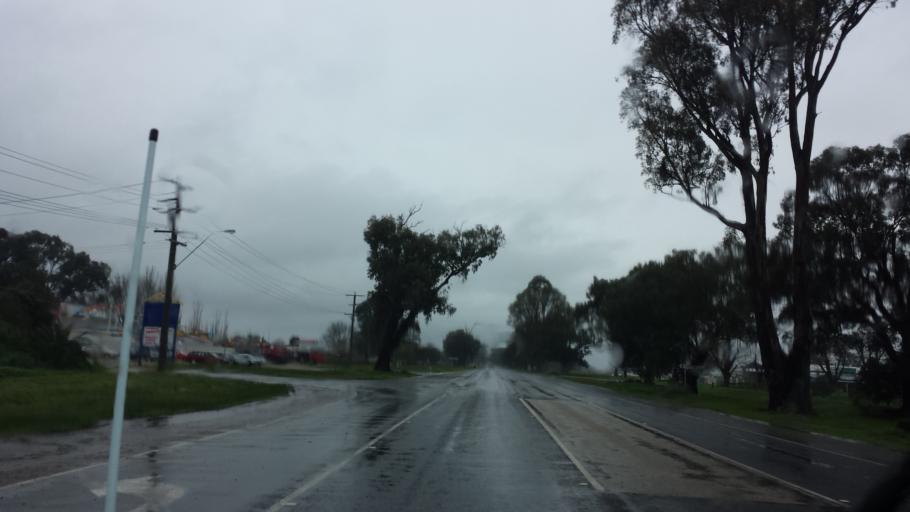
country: AU
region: Victoria
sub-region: Benalla
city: Benalla
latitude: -36.5428
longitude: 146.0108
